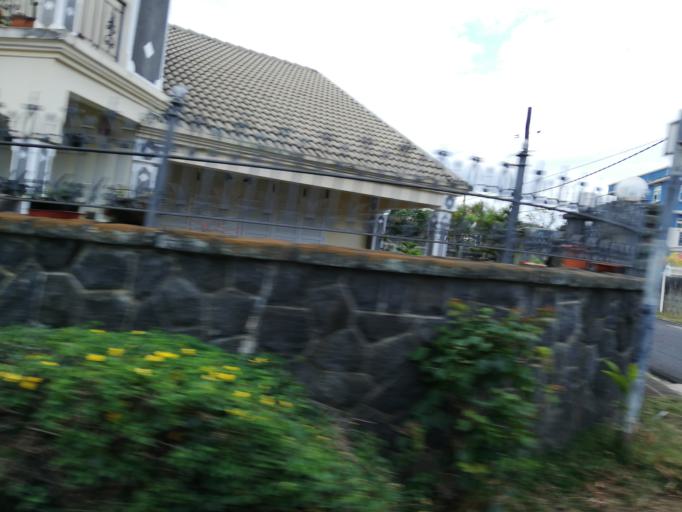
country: MU
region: Black River
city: Gros Cailloux
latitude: -20.2347
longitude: 57.4554
